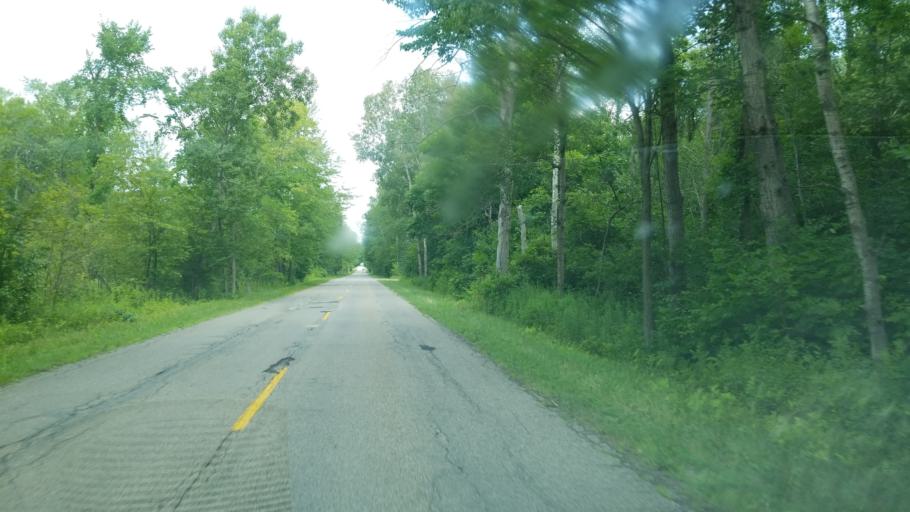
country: US
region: Michigan
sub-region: Kent County
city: Cedar Springs
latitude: 43.2411
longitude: -85.5111
